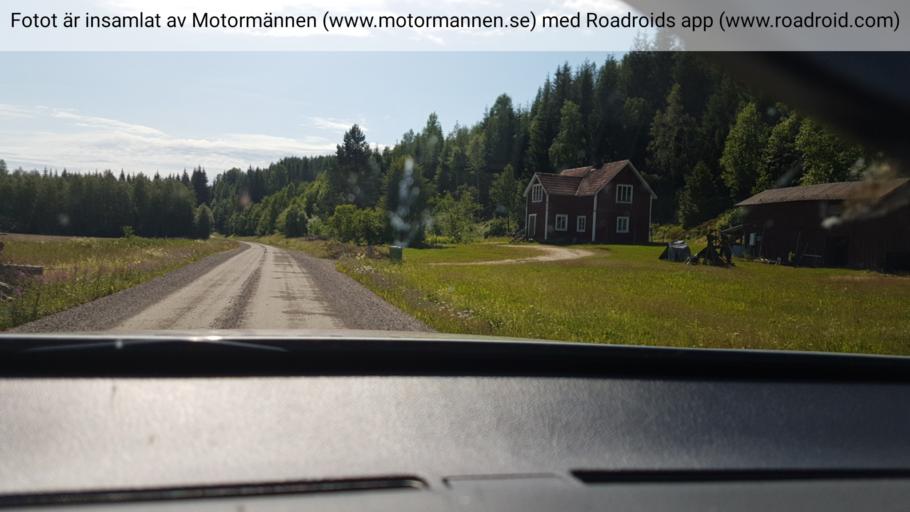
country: SE
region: Vaermland
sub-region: Torsby Kommun
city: Torsby
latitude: 60.5399
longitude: 13.1084
